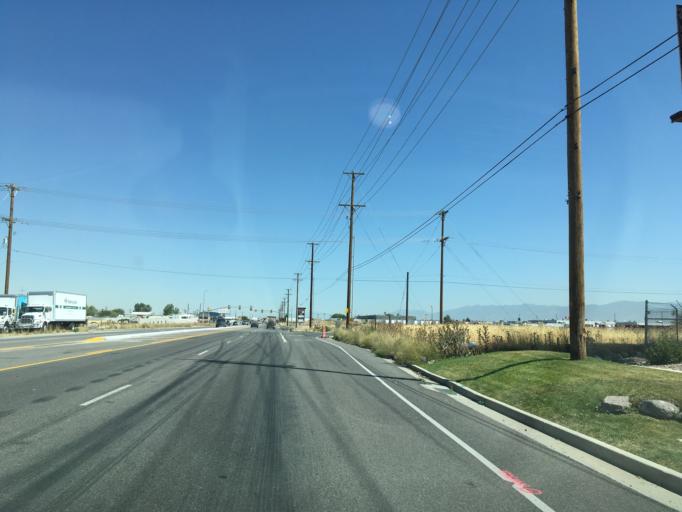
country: US
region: Utah
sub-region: Salt Lake County
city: West Valley City
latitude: 40.7160
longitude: -112.0248
